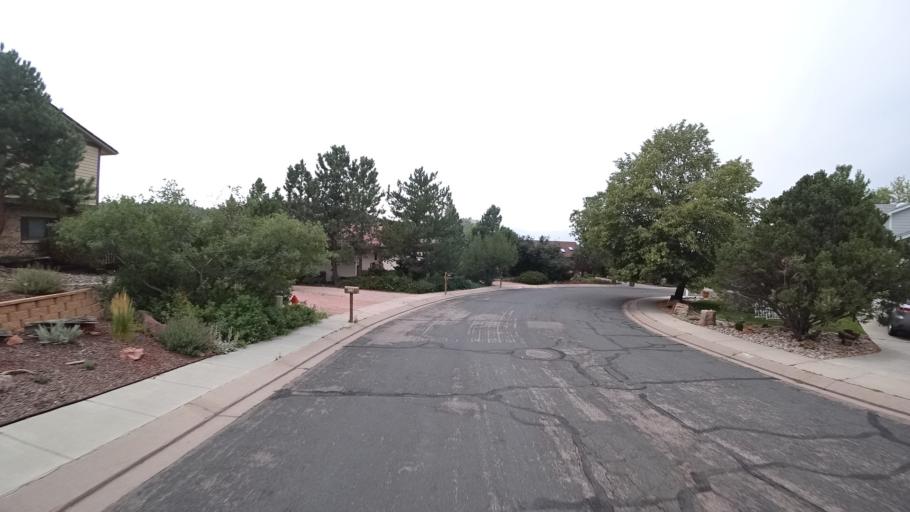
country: US
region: Colorado
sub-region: El Paso County
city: Colorado Springs
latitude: 38.9196
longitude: -104.8087
